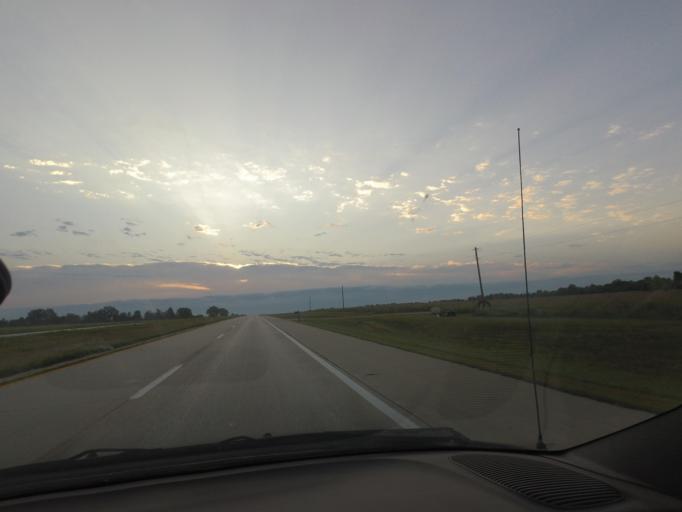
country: US
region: Missouri
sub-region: Macon County
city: Macon
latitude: 39.7502
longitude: -92.3546
